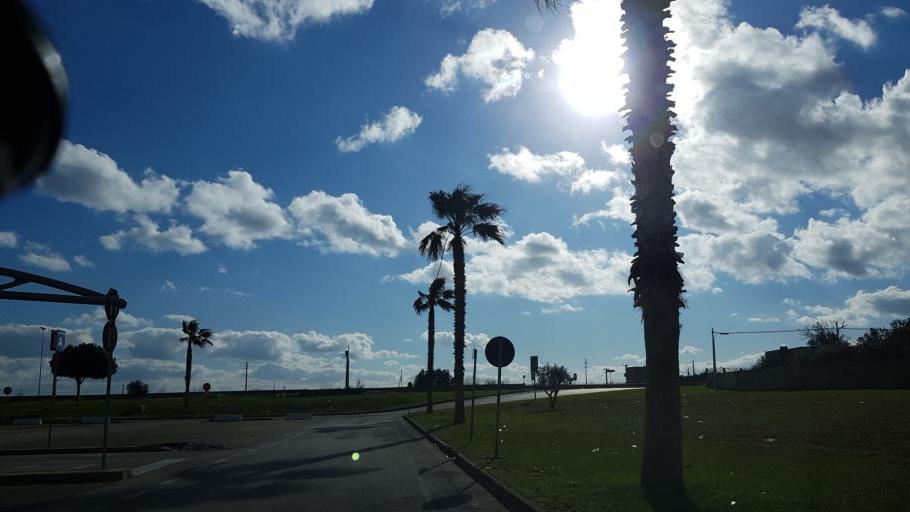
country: IT
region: Apulia
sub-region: Provincia di Brindisi
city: Brindisi
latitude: 40.6168
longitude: 17.9019
